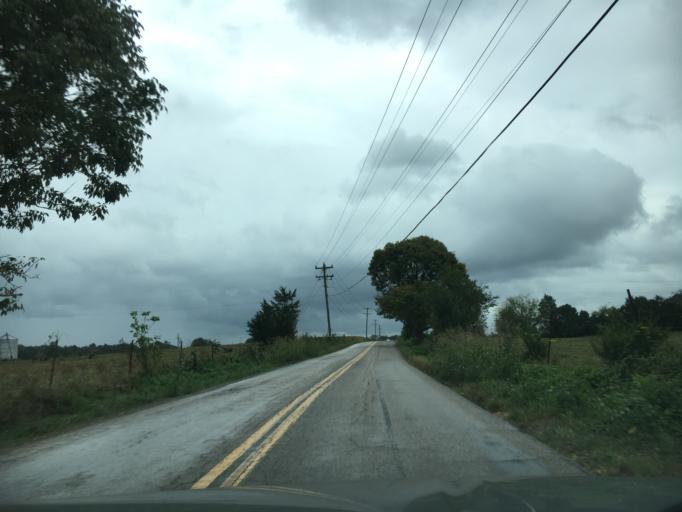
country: US
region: Virginia
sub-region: Amelia County
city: Amelia Court House
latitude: 37.3906
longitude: -77.9769
